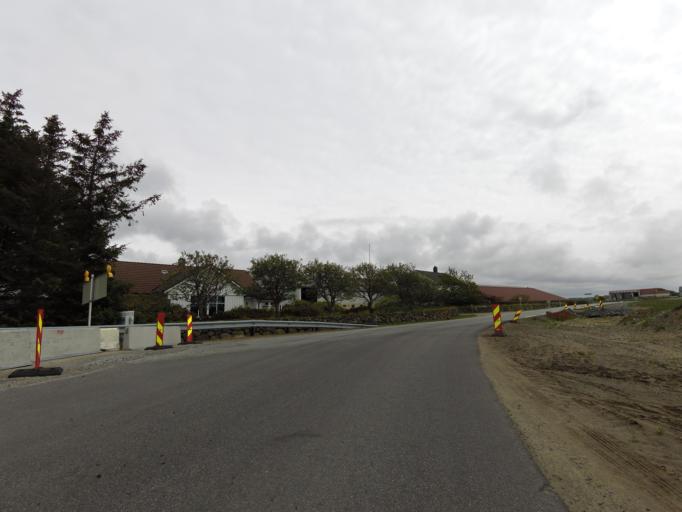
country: NO
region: Rogaland
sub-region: Ha
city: Naerbo
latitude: 58.6866
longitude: 5.5613
